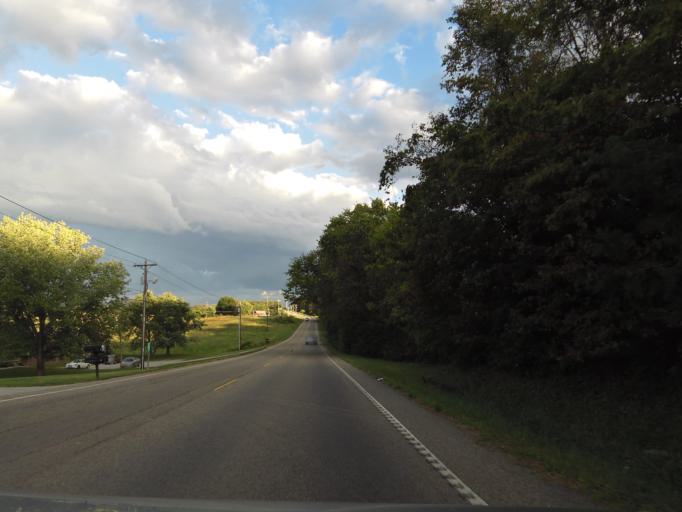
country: US
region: Tennessee
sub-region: Jefferson County
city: Jefferson City
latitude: 36.1249
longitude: -83.5155
